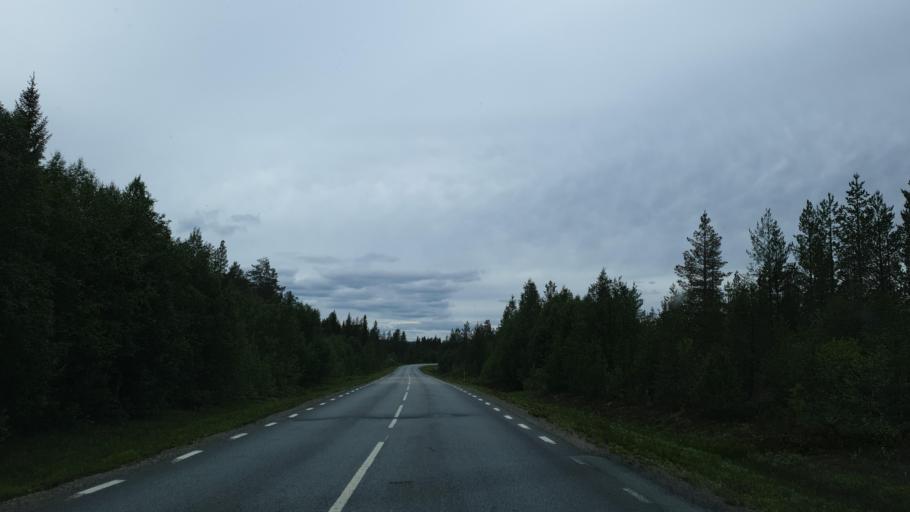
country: SE
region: Vaesterbotten
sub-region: Sorsele Kommun
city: Sorsele
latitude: 65.5182
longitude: 17.1872
